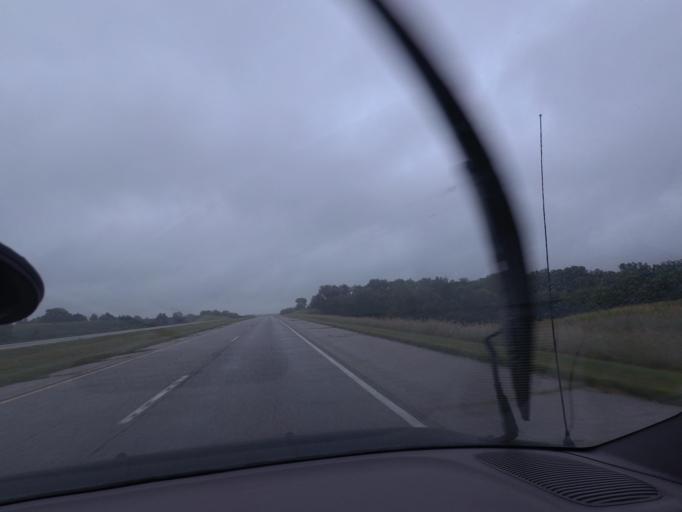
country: US
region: Illinois
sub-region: Pike County
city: Barry
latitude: 39.6927
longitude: -90.9660
